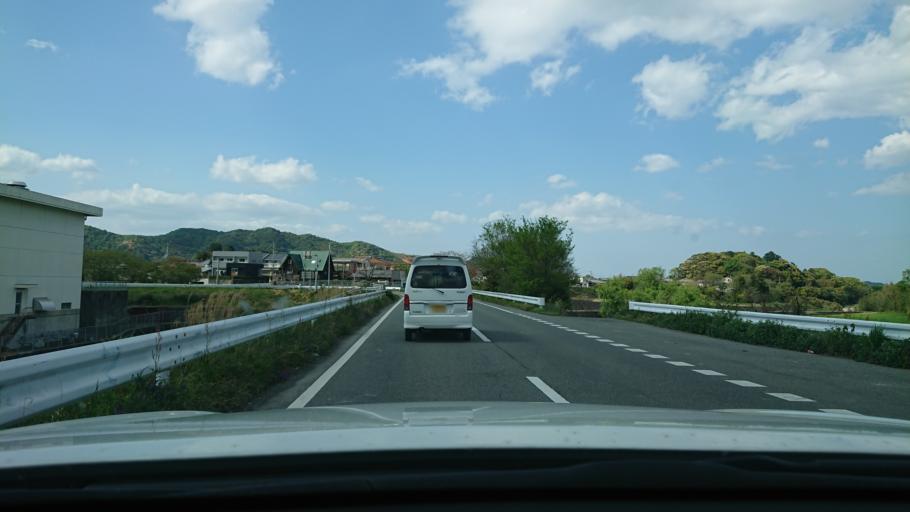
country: JP
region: Tokushima
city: Komatsushimacho
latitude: 33.9994
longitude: 134.5475
